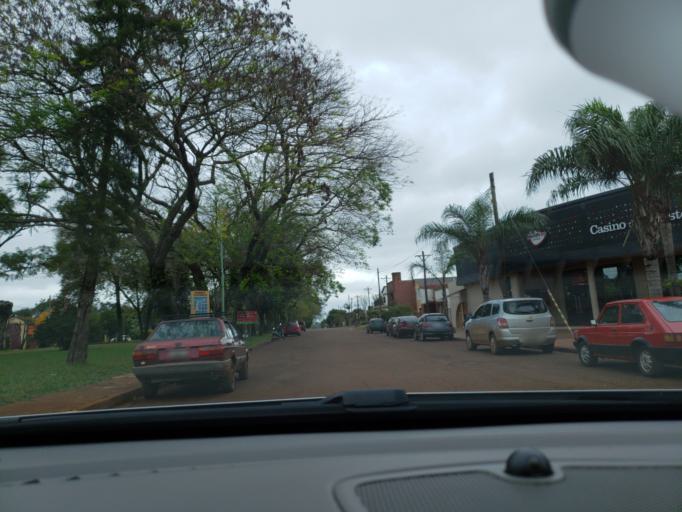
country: AR
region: Misiones
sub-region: Departamento de Apostoles
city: Apostoles
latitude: -27.9206
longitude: -55.7624
